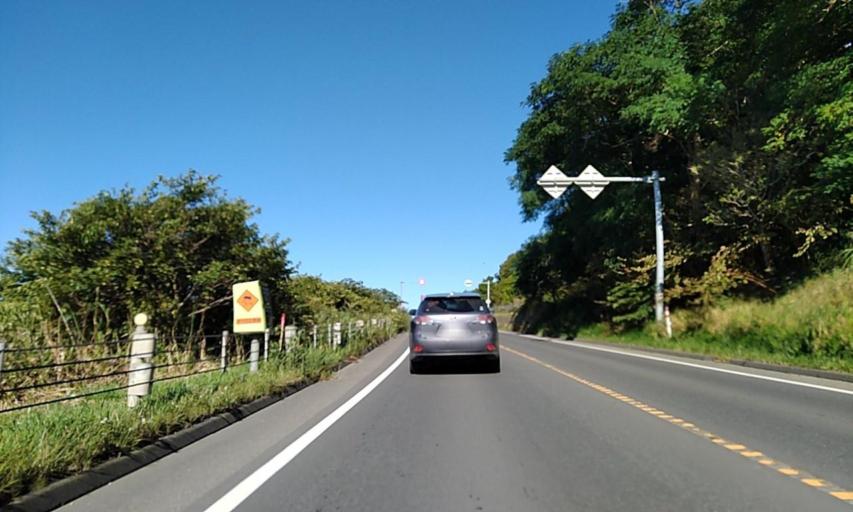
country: JP
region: Hokkaido
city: Shizunai-furukawacho
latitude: 42.3830
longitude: 142.2769
